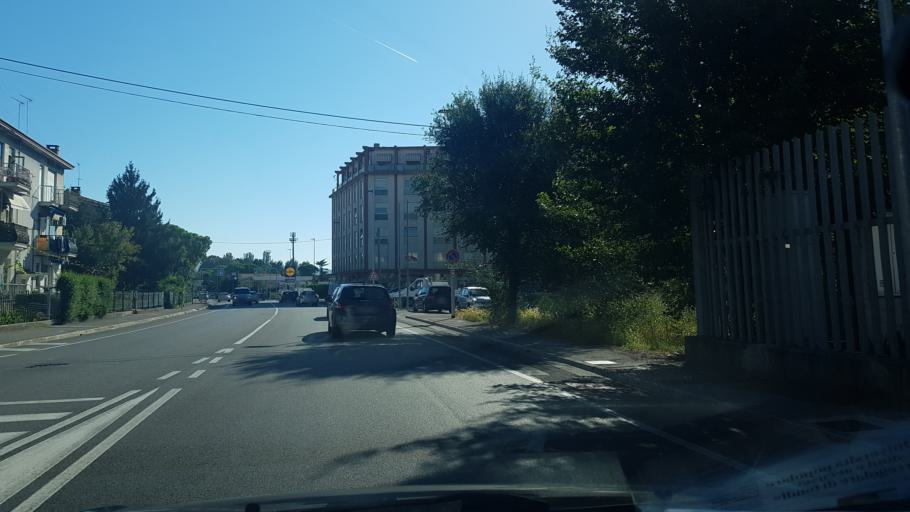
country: IT
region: Friuli Venezia Giulia
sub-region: Provincia di Gorizia
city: Monfalcone
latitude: 45.8028
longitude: 13.5392
